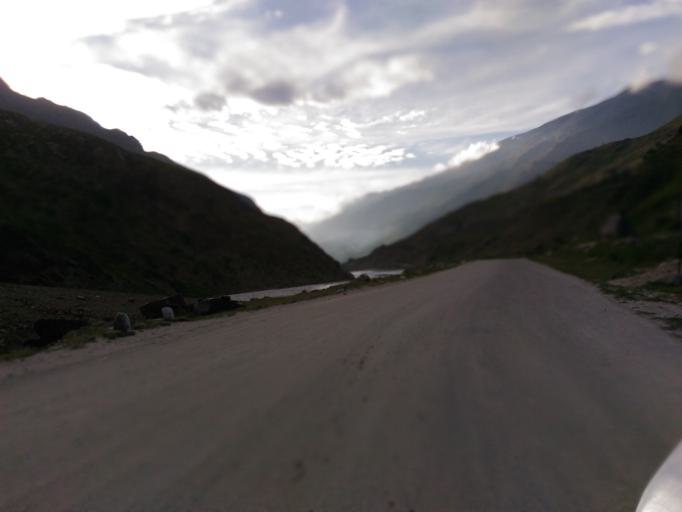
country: IN
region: Himachal Pradesh
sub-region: Lahul and Spiti
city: Kyelang
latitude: 32.4500
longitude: 77.1532
